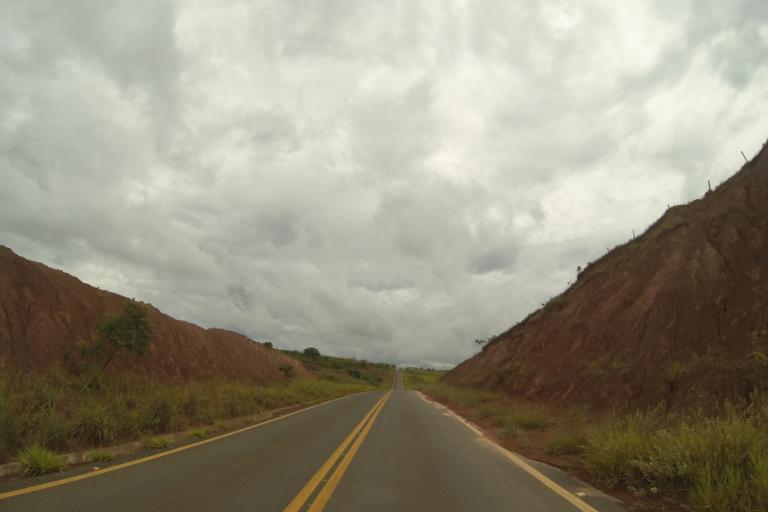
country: BR
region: Minas Gerais
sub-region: Bambui
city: Bambui
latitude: -20.0870
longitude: -46.1347
